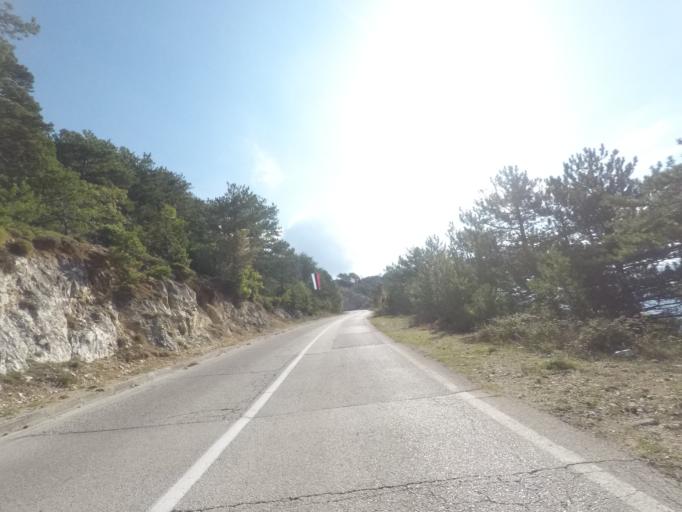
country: BA
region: Republika Srpska
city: Trebinje
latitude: 42.7135
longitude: 18.5370
